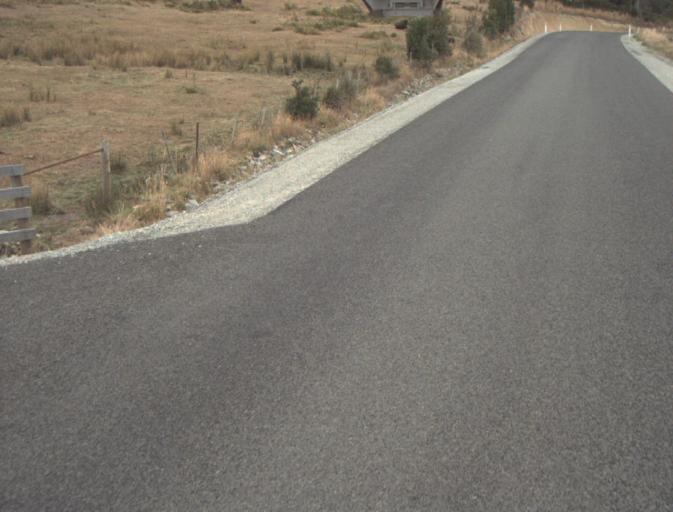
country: AU
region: Tasmania
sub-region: Launceston
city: Mayfield
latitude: -41.1996
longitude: 147.1878
